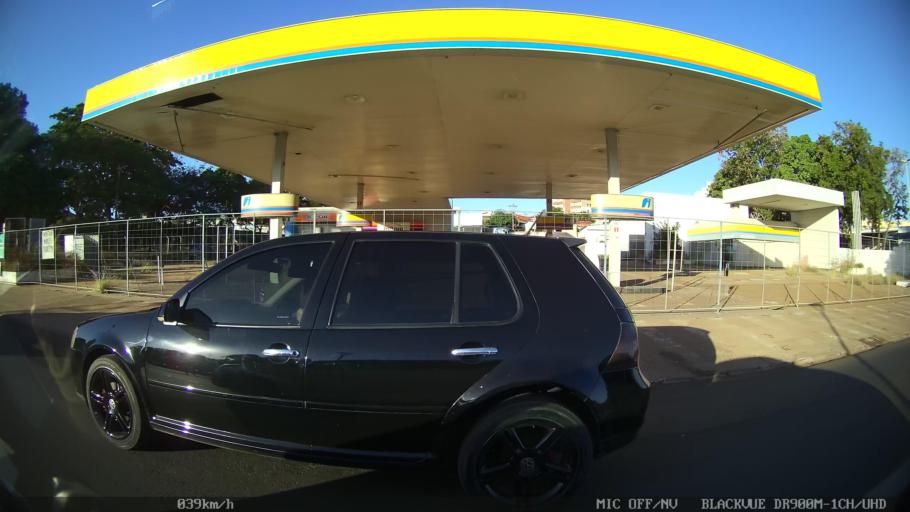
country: BR
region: Sao Paulo
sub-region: Sao Jose Do Rio Preto
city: Sao Jose do Rio Preto
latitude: -20.8050
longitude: -49.3771
